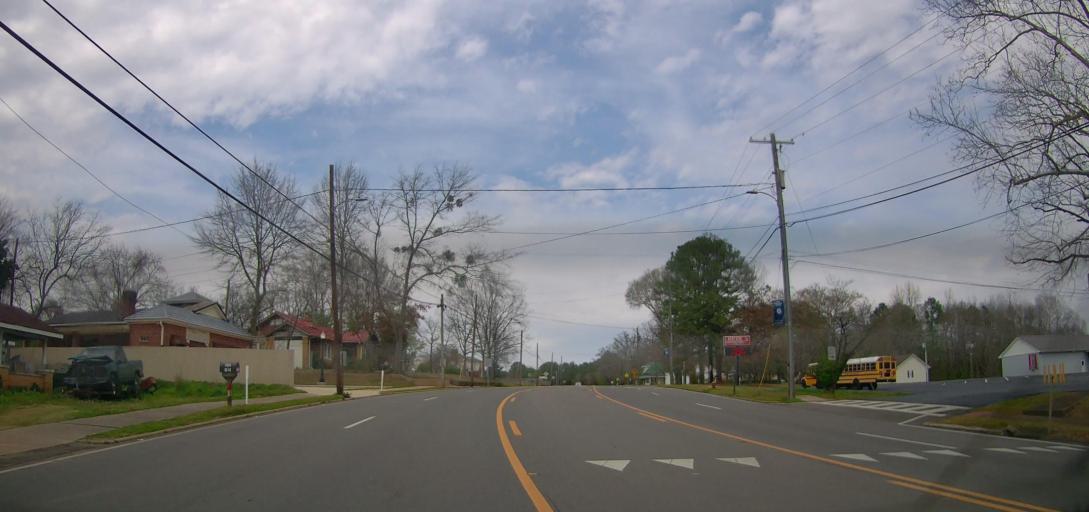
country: US
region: Alabama
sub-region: Marion County
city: Guin
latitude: 33.9716
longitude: -87.9157
